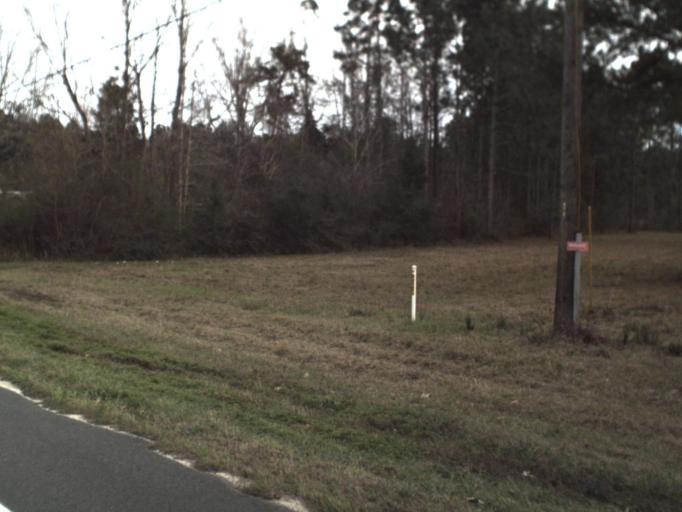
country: US
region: Florida
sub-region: Gulf County
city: Wewahitchka
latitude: 30.1232
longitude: -85.2186
